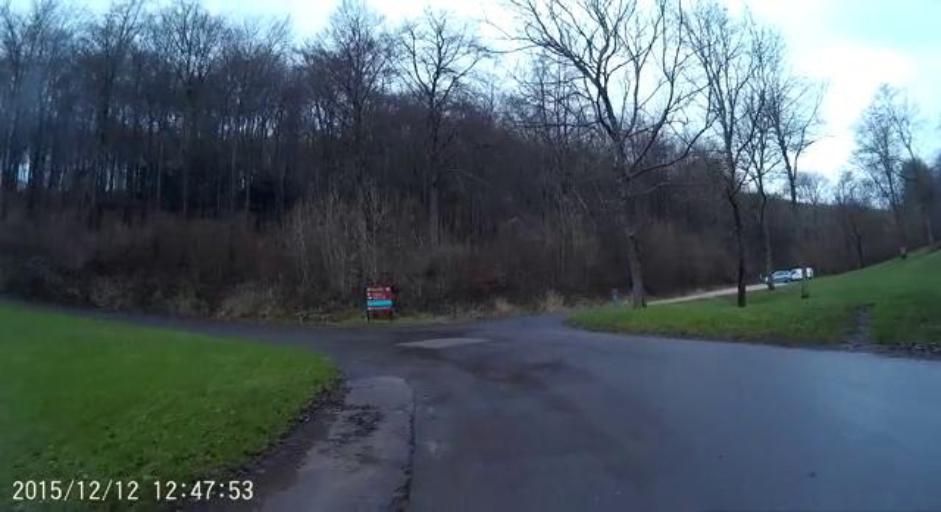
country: GB
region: England
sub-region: Hampshire
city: Petersfield
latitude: 50.9607
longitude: -0.9729
